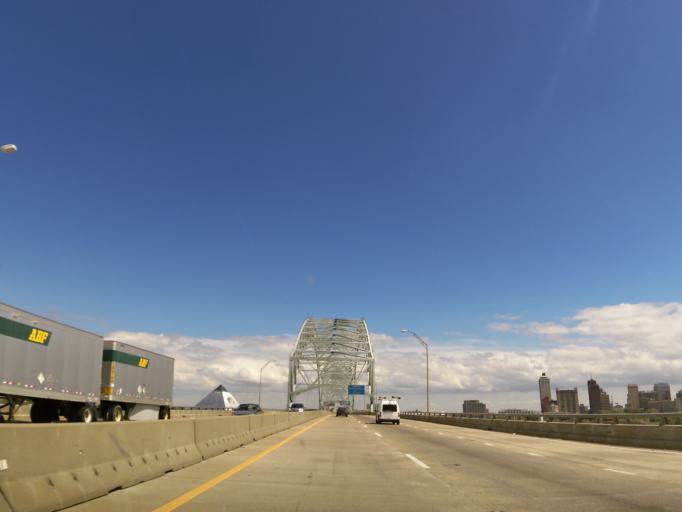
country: US
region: Tennessee
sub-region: Shelby County
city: Memphis
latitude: 35.1530
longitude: -90.0666
